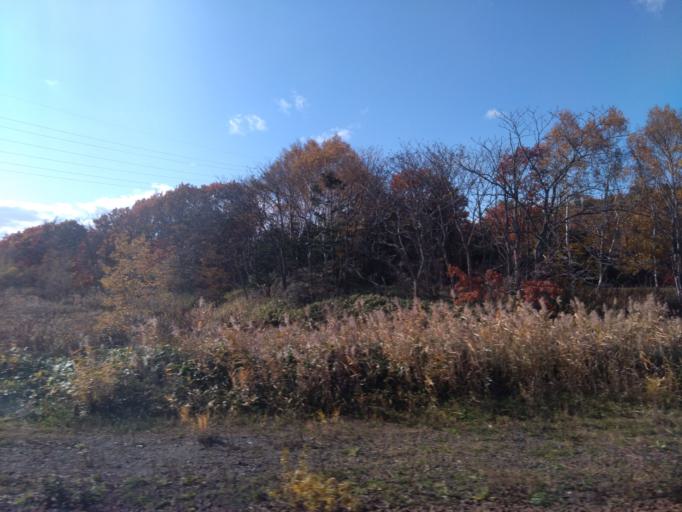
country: JP
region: Hokkaido
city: Kitahiroshima
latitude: 42.9441
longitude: 141.5717
